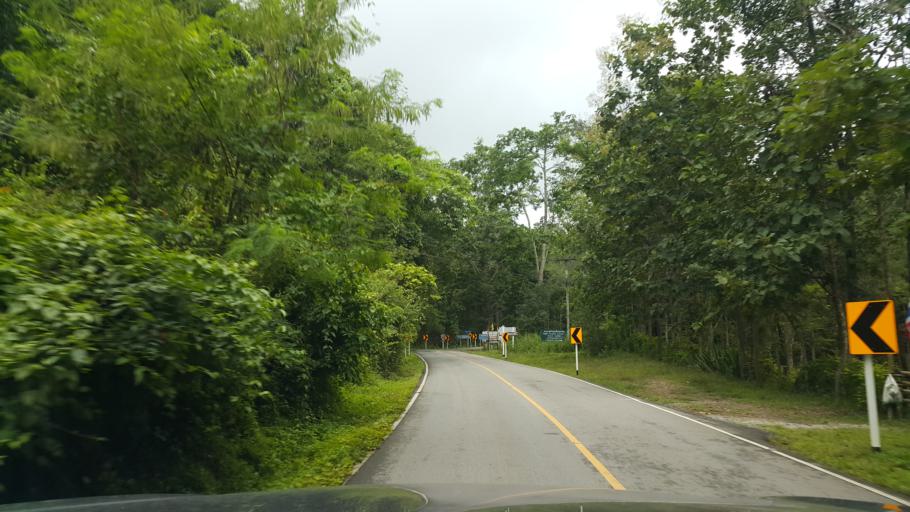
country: TH
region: Chiang Mai
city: Samoeng
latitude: 18.8654
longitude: 98.6295
